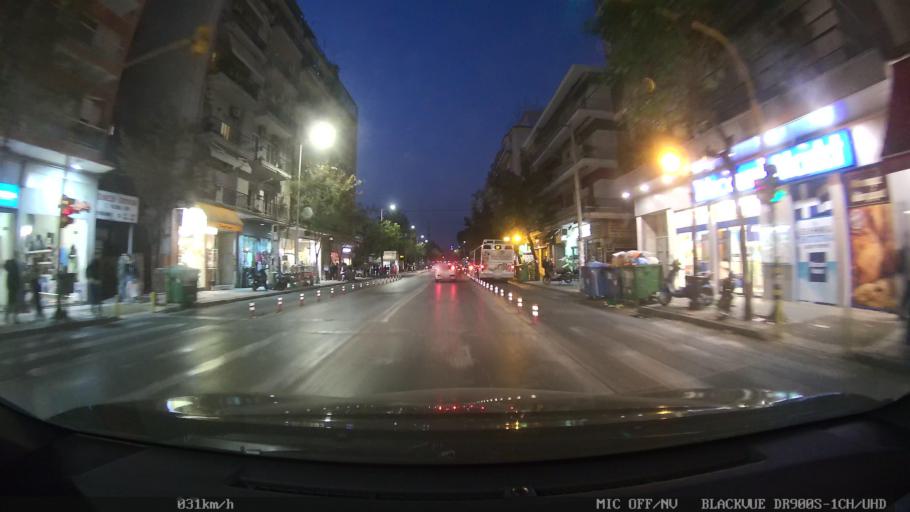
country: GR
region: Central Macedonia
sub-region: Nomos Thessalonikis
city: Triandria
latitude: 40.6204
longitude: 22.9576
